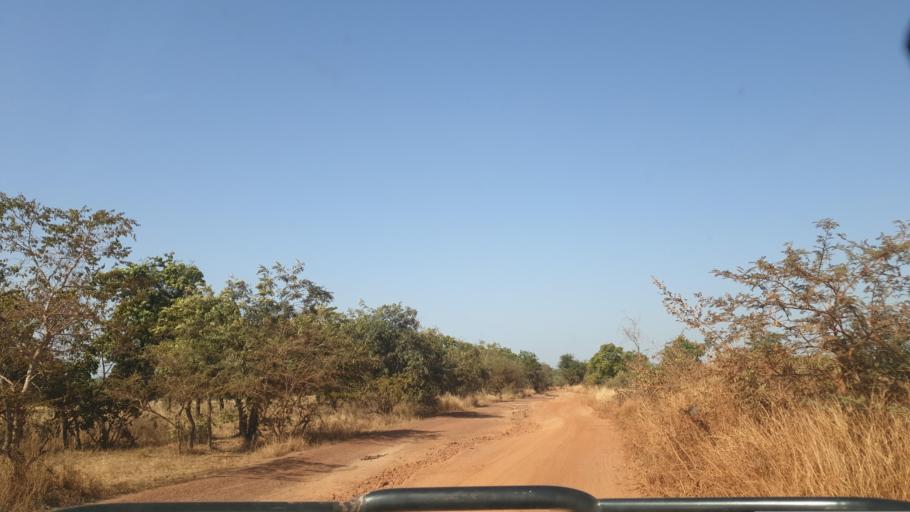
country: ML
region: Sikasso
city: Bougouni
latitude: 11.8208
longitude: -6.9648
